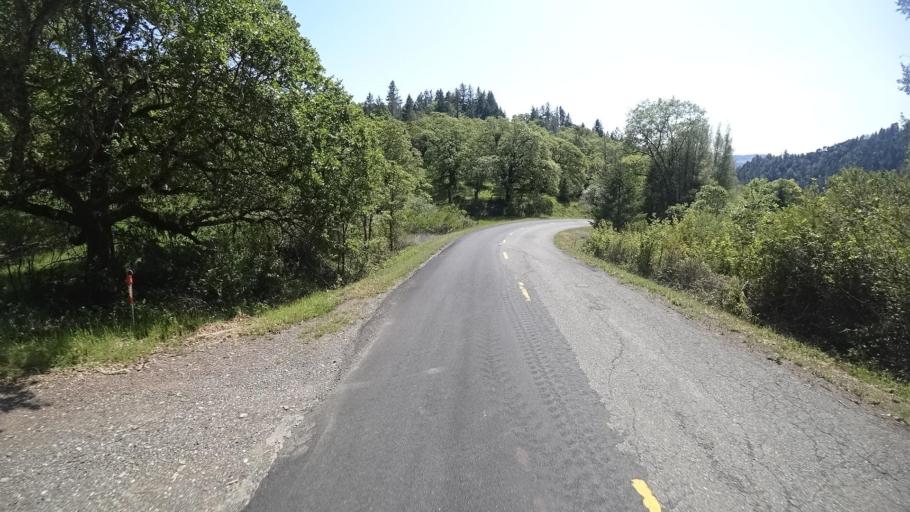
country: US
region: California
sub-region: Humboldt County
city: Redway
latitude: 40.2680
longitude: -123.6254
